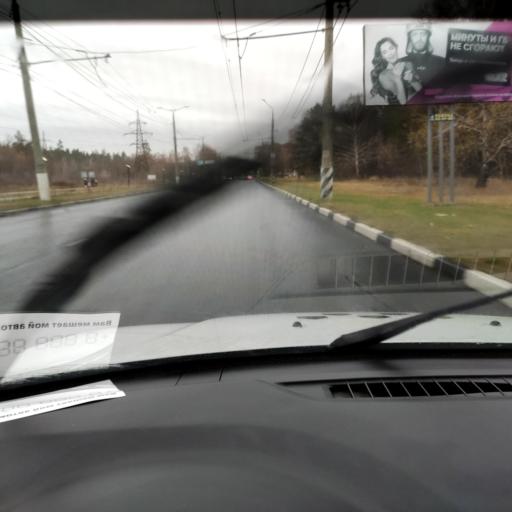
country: RU
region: Samara
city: Tol'yatti
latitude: 53.4965
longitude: 49.3876
